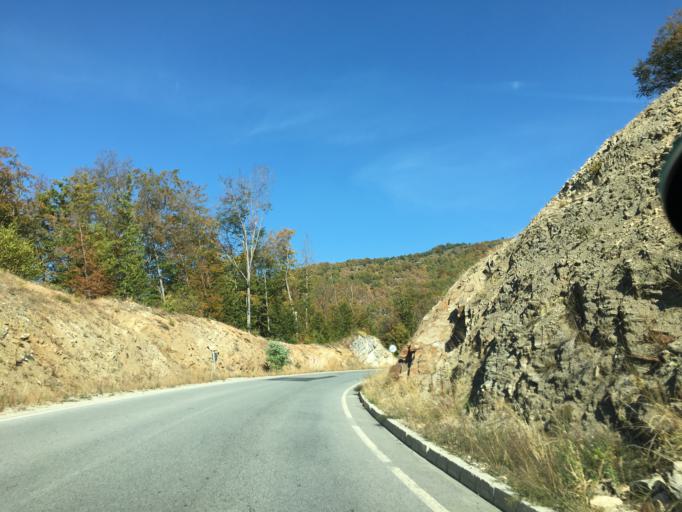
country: BG
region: Smolyan
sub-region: Obshtina Devin
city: Devin
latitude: 41.7748
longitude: 24.4493
